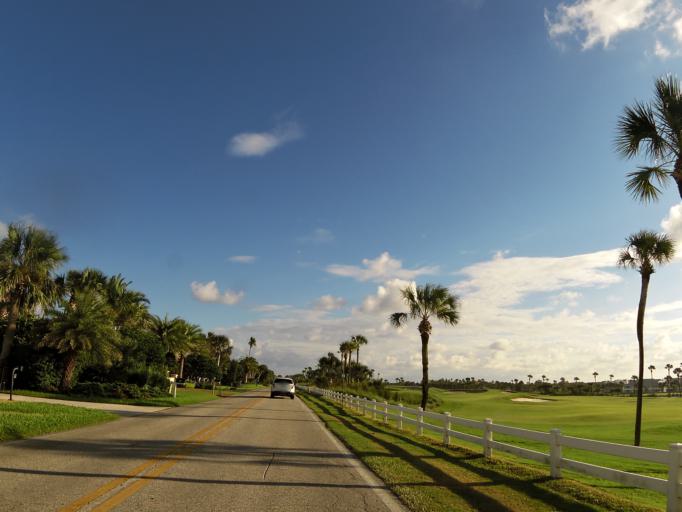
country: US
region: Florida
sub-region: Saint Johns County
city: Ponte Vedra Beach
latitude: 30.2495
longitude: -81.3808
